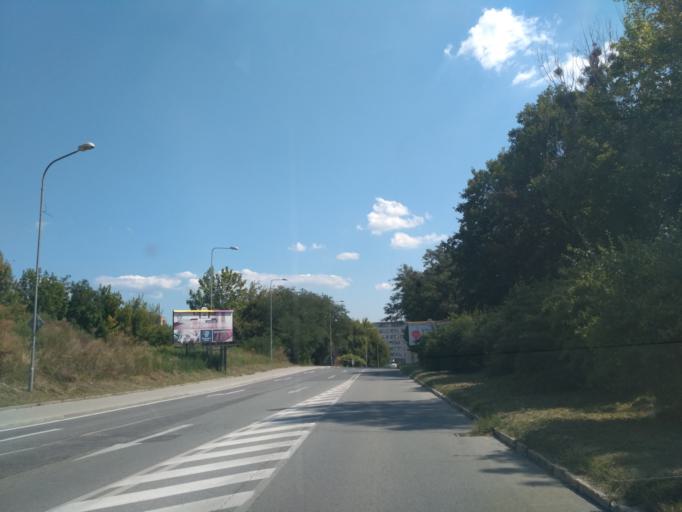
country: SK
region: Kosicky
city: Kosice
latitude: 48.7203
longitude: 21.2415
